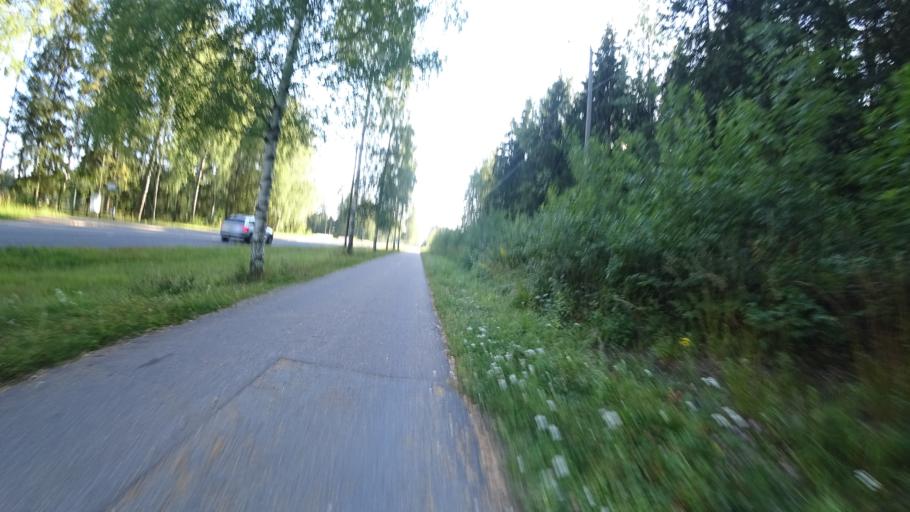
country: FI
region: Pirkanmaa
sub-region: Tampere
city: Nokia
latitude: 61.4726
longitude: 23.4680
